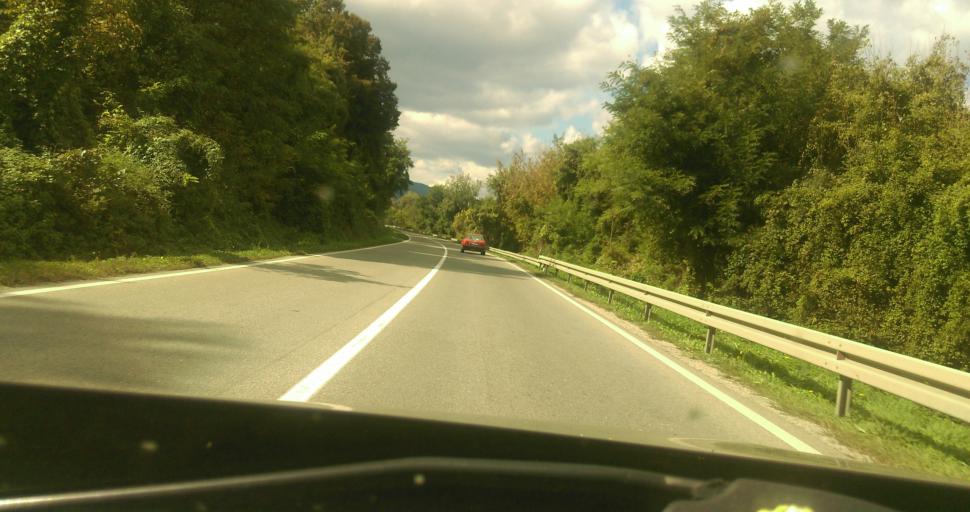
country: RS
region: Central Serbia
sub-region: Moravicki Okrug
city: Cacak
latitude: 43.8983
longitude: 20.2789
